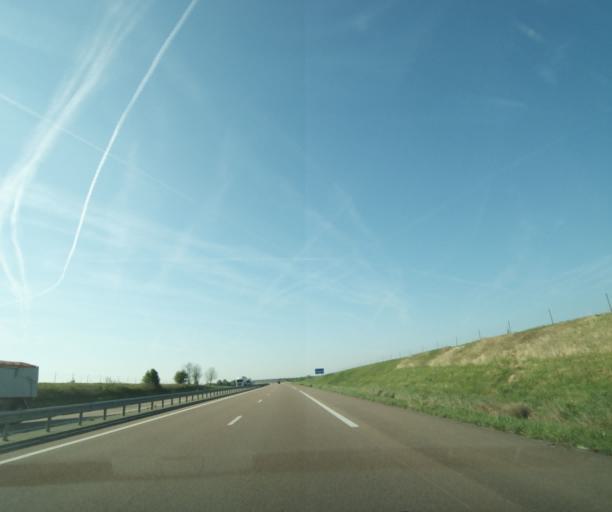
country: FR
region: Ile-de-France
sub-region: Departement de Seine-et-Marne
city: Souppes-sur-Loing
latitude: 48.1942
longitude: 2.7683
